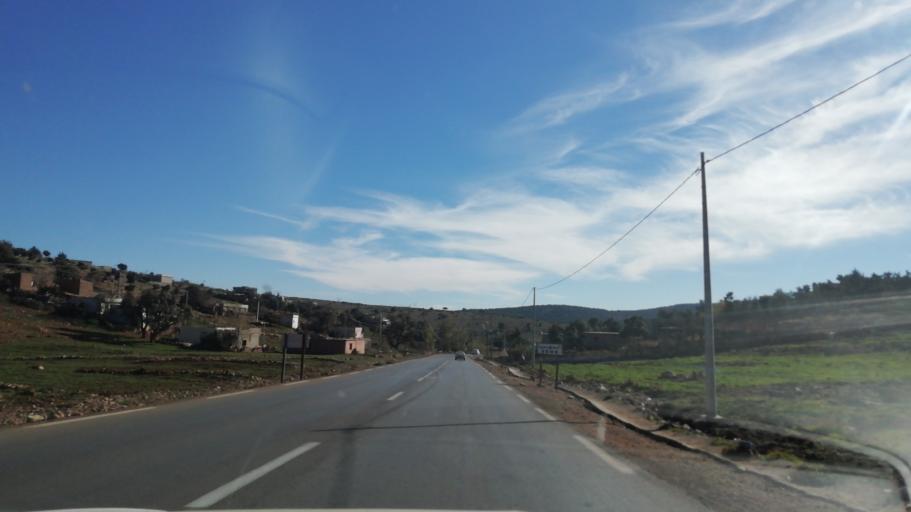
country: DZ
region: Tlemcen
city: Sebdou
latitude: 34.7310
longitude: -1.3379
